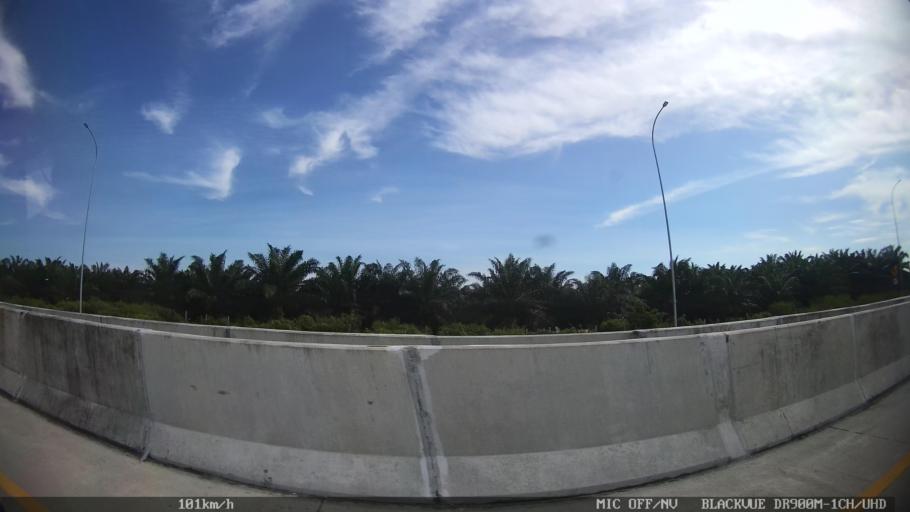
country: ID
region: North Sumatra
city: Binjai
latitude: 3.6478
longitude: 98.5466
